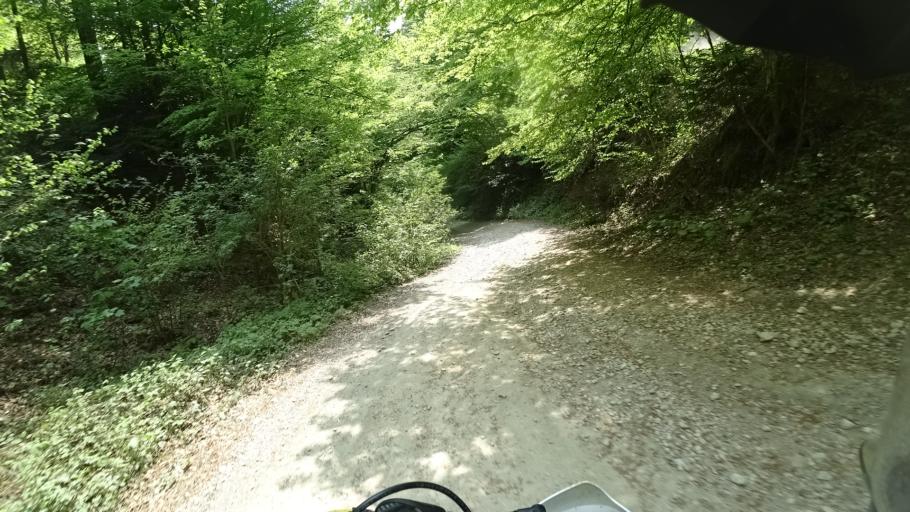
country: HR
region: Grad Zagreb
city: Kasina
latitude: 45.9252
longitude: 16.0236
